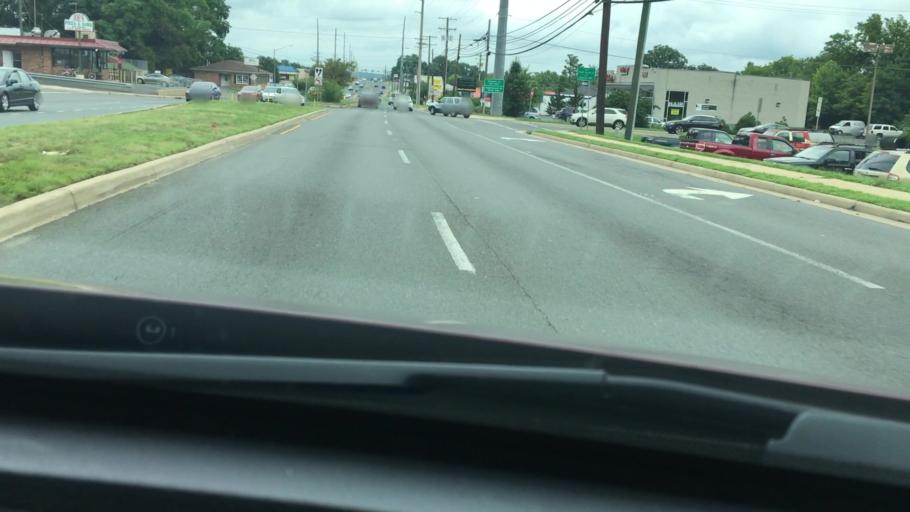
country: US
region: Virginia
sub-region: City of Manassas Park
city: Manassas Park
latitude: 38.7729
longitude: -77.4523
